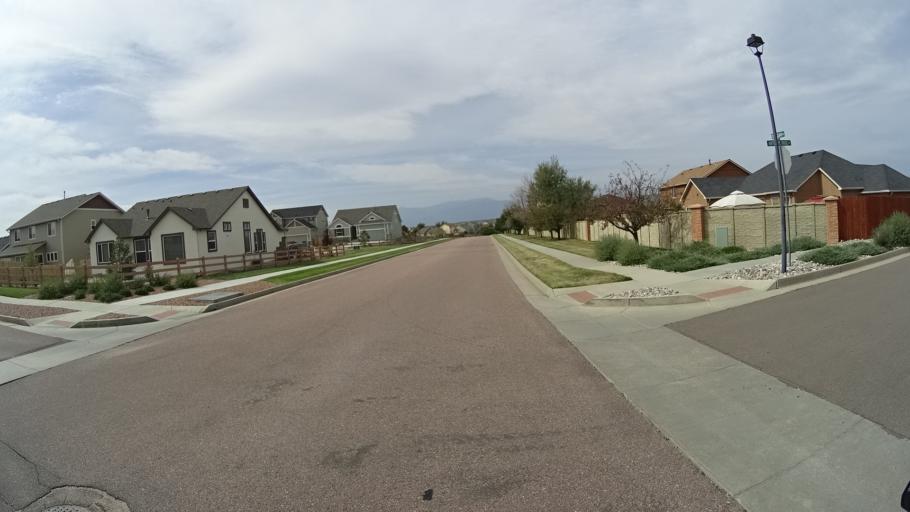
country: US
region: Colorado
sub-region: El Paso County
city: Cimarron Hills
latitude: 38.9192
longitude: -104.6867
